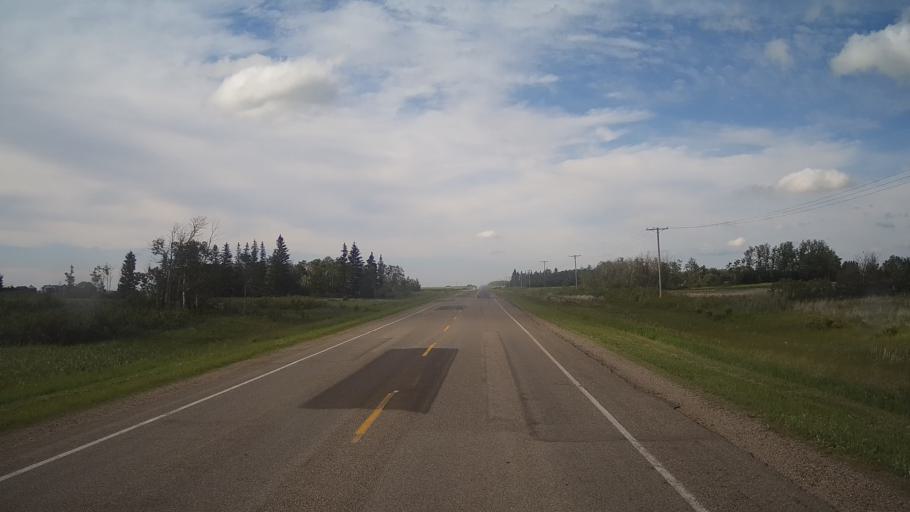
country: CA
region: Saskatchewan
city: Foam Lake
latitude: 51.6000
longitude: -103.8459
